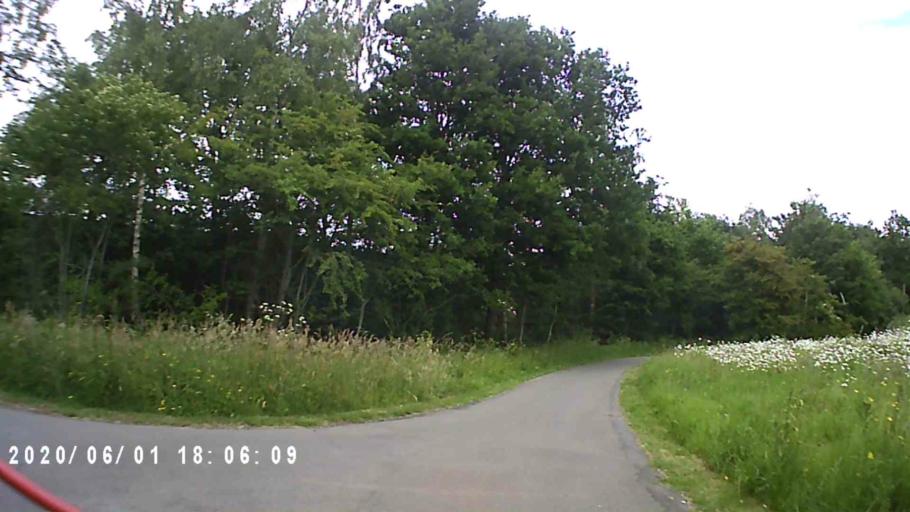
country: NL
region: Friesland
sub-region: Gemeente Tytsjerksteradiel
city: Sumar
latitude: 53.1793
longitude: 5.9948
